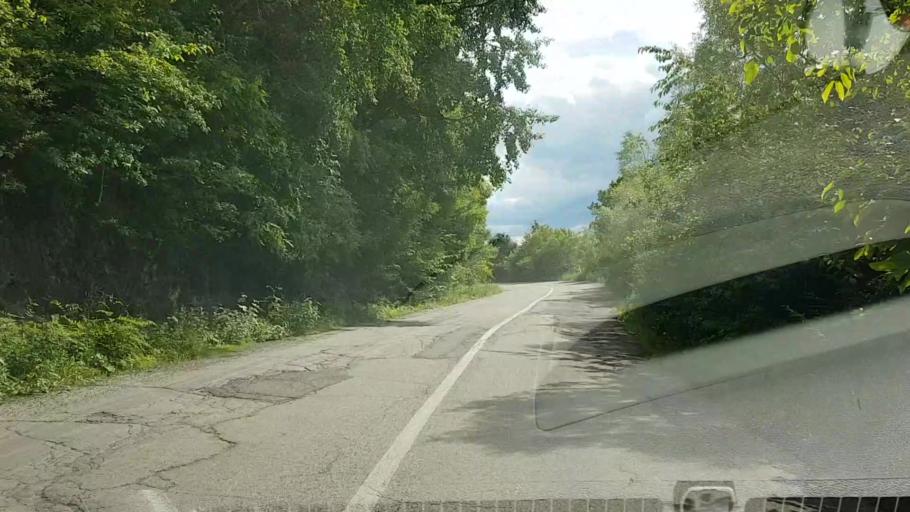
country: RO
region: Neamt
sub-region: Comuna Hangu
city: Hangu
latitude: 47.0274
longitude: 26.0680
